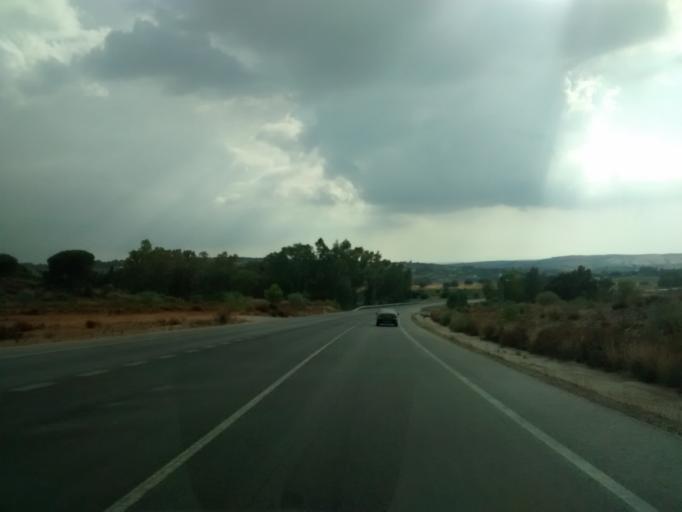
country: ES
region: Andalusia
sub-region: Provincia de Cadiz
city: Arcos de la Frontera
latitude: 36.7525
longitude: -5.7509
